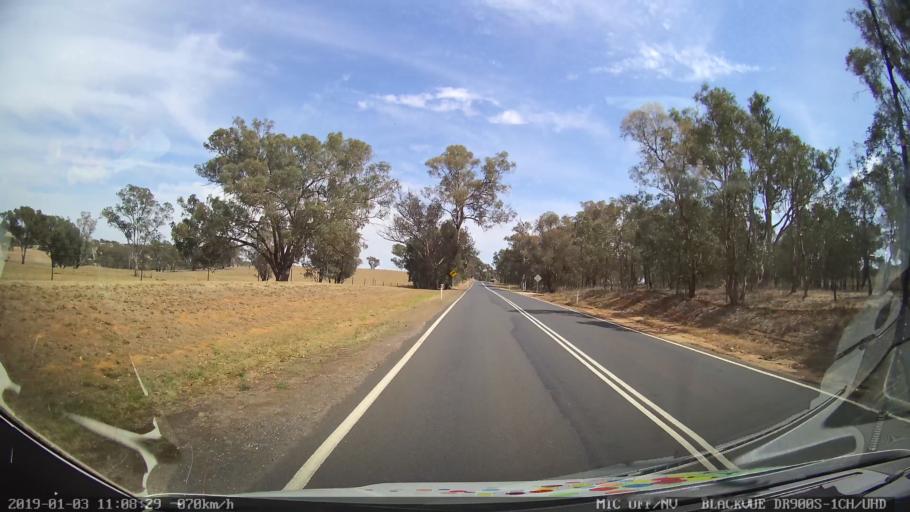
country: AU
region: New South Wales
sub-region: Young
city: Young
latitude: -34.2488
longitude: 148.2569
